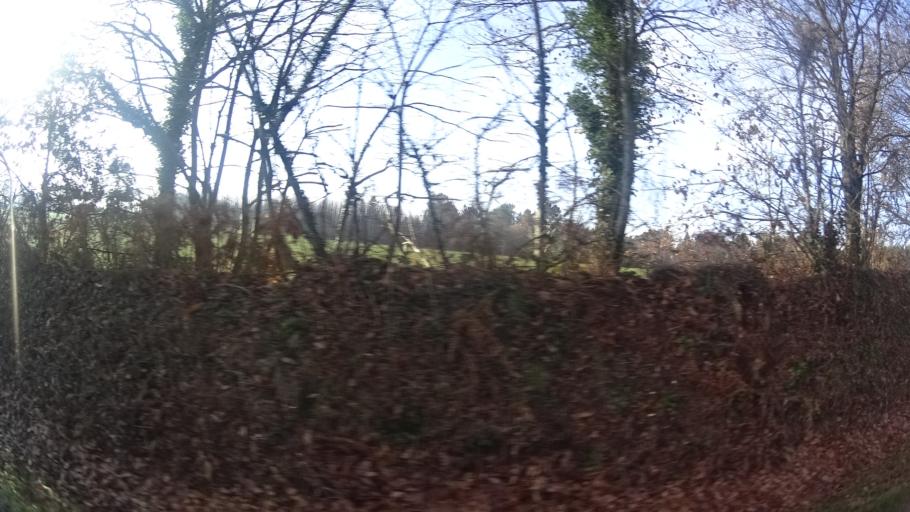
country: FR
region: Brittany
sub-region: Departement du Morbihan
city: Allaire
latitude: 47.6176
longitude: -2.1498
